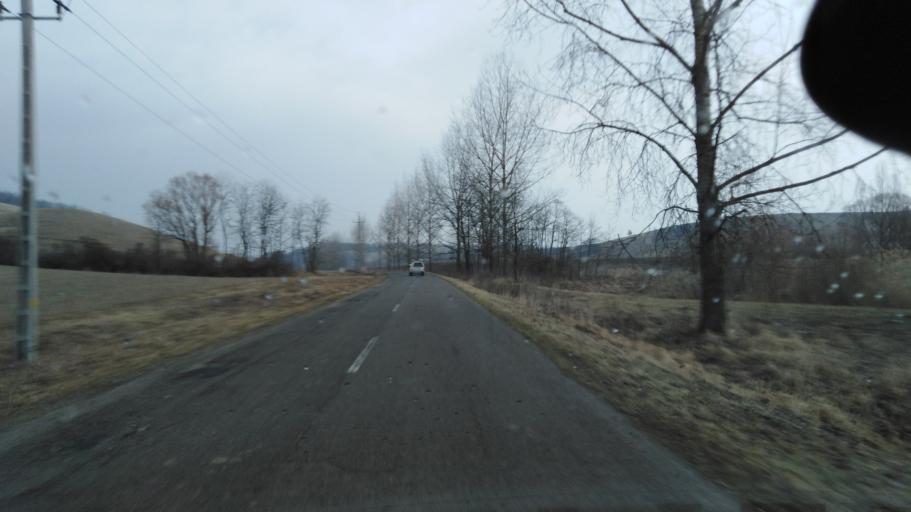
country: HU
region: Nograd
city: Matraverebely
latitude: 48.0419
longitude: 19.7398
